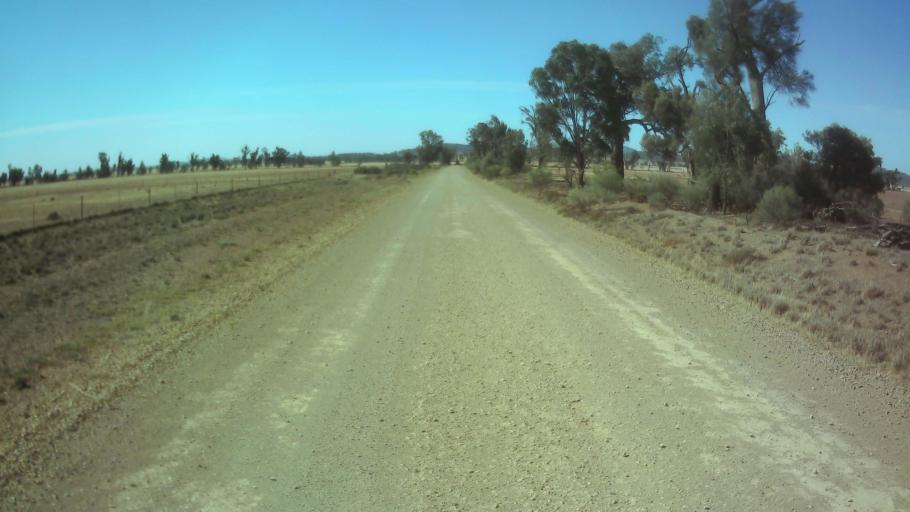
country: AU
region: New South Wales
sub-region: Forbes
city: Forbes
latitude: -33.7099
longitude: 147.7471
